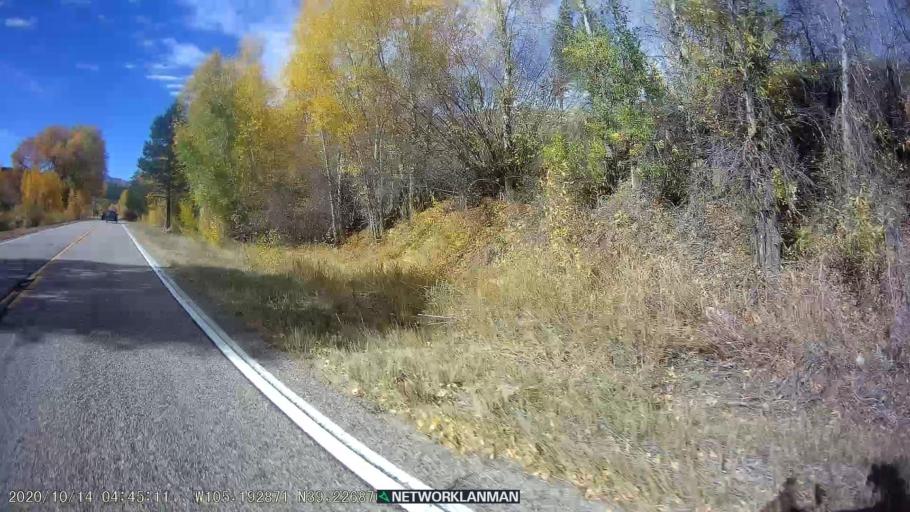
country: US
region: Colorado
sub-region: Douglas County
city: Perry Park
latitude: 39.2269
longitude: -105.1929
